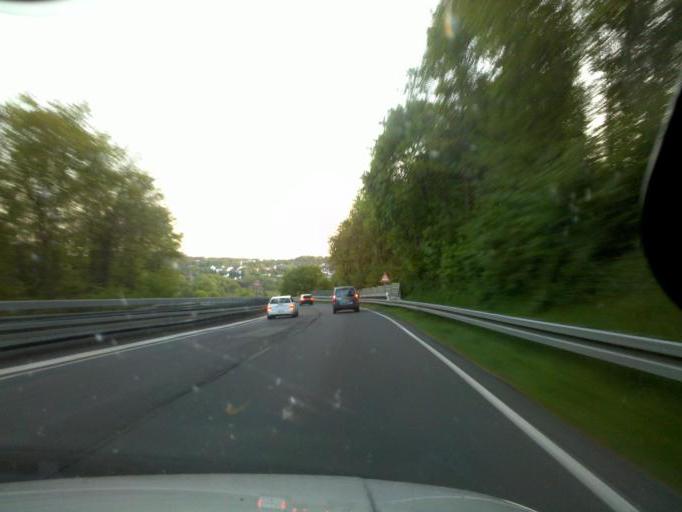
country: DE
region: North Rhine-Westphalia
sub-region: Regierungsbezirk Koln
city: Gummersbach
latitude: 50.9900
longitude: 7.5502
